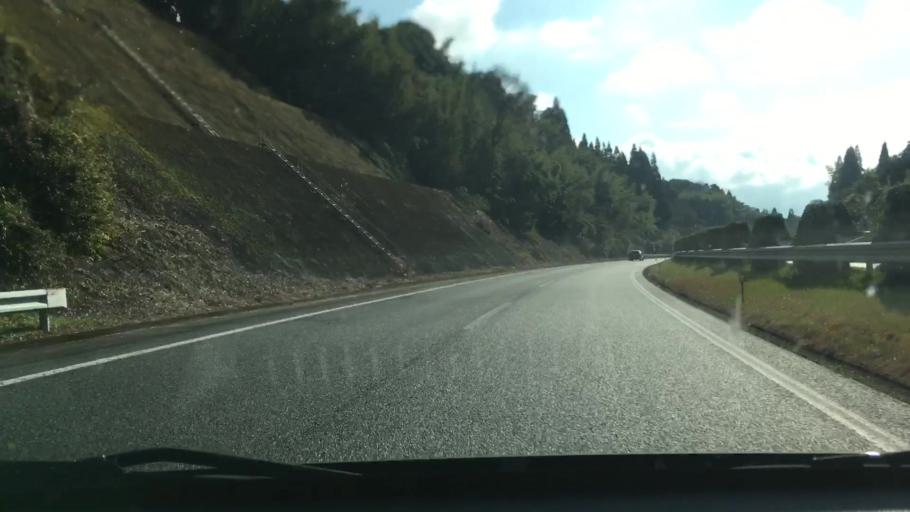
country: JP
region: Kumamoto
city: Matsubase
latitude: 32.6099
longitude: 130.7246
